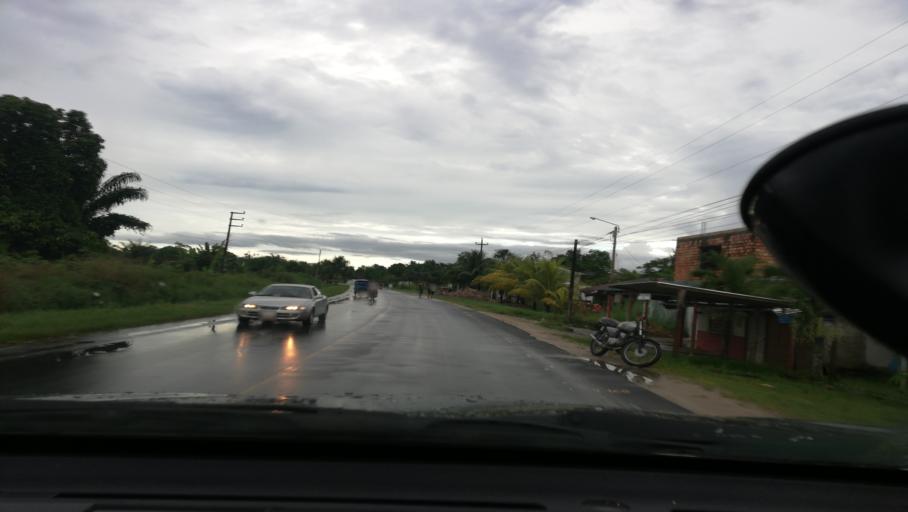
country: PE
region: Loreto
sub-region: Provincia de Maynas
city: Iquitos
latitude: -3.8486
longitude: -73.3381
